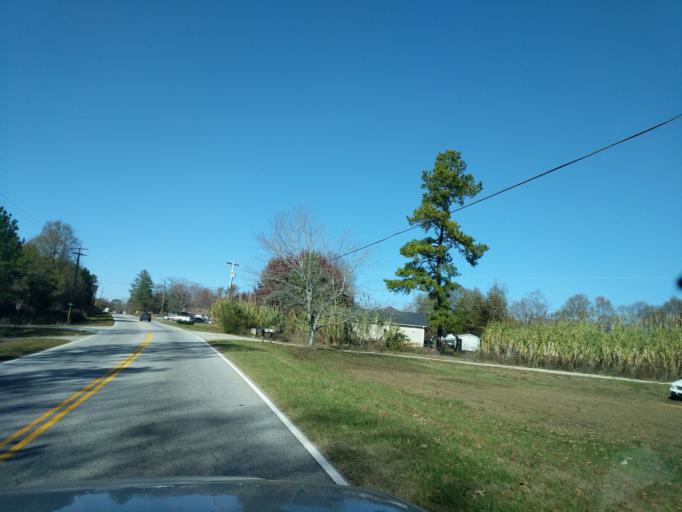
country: US
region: South Carolina
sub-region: Greenville County
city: Taylors
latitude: 34.9833
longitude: -82.3342
